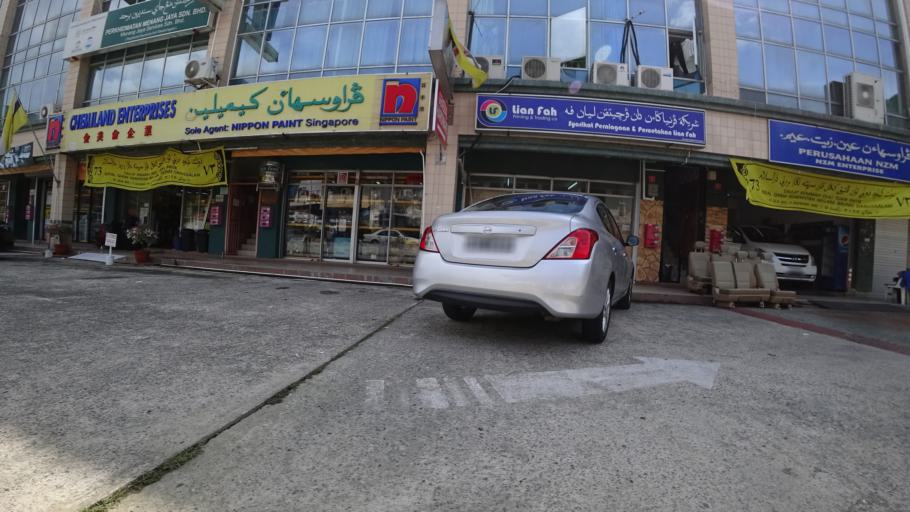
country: BN
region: Brunei and Muara
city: Bandar Seri Begawan
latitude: 4.8577
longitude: 114.8925
